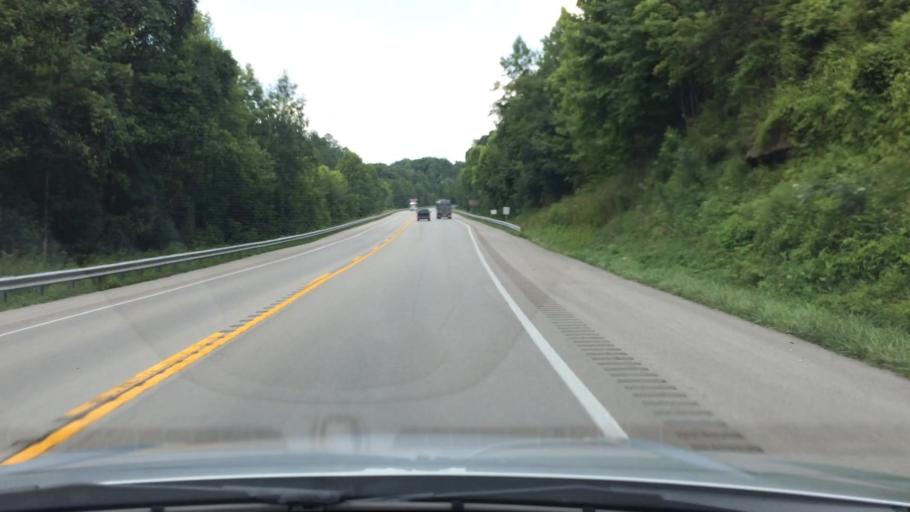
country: US
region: Kentucky
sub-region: McCreary County
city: Whitley City
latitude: 36.9038
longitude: -84.5024
